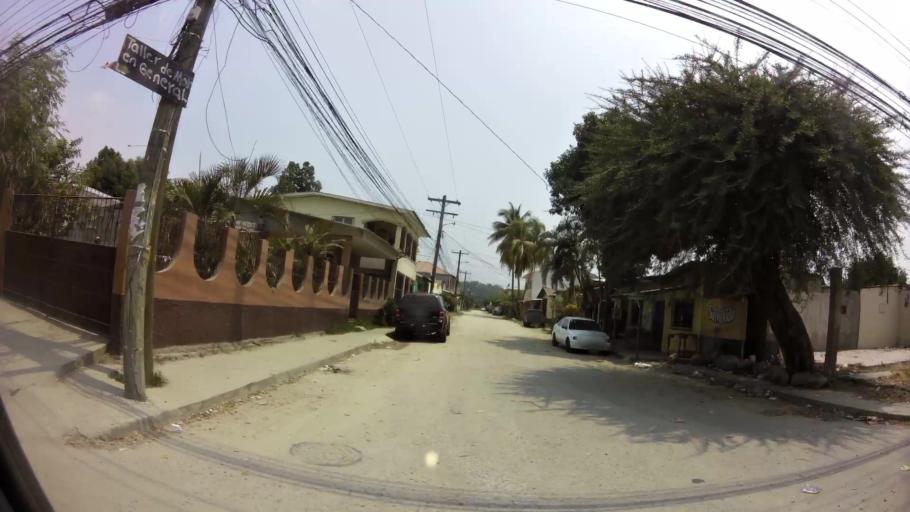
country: HN
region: Cortes
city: San Pedro Sula
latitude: 15.4909
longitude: -87.9937
